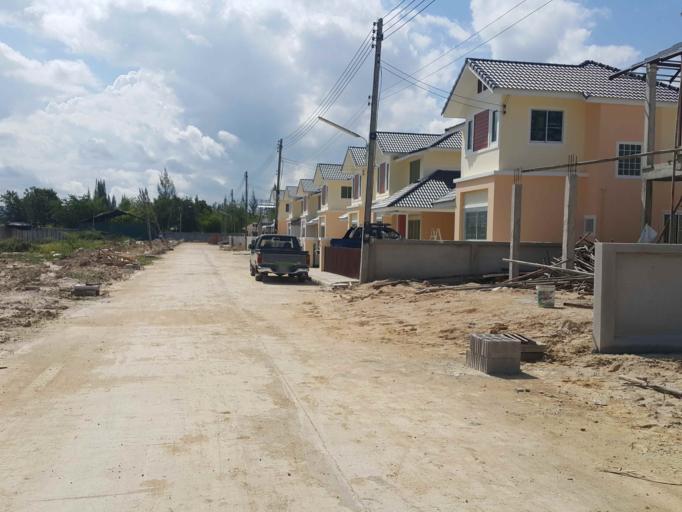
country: TH
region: Chiang Mai
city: San Kamphaeng
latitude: 18.7785
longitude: 99.0835
